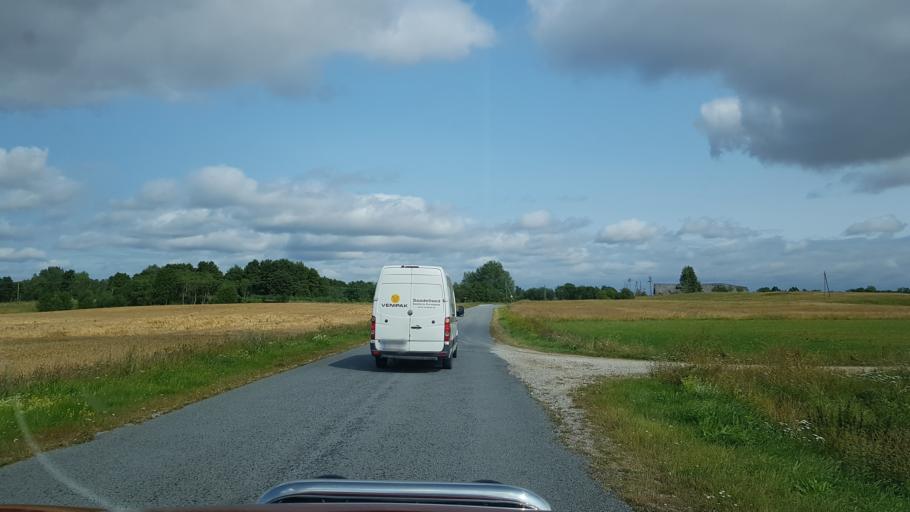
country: EE
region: Laeaene-Virumaa
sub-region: Kadrina vald
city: Kadrina
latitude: 59.3401
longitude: 26.0796
